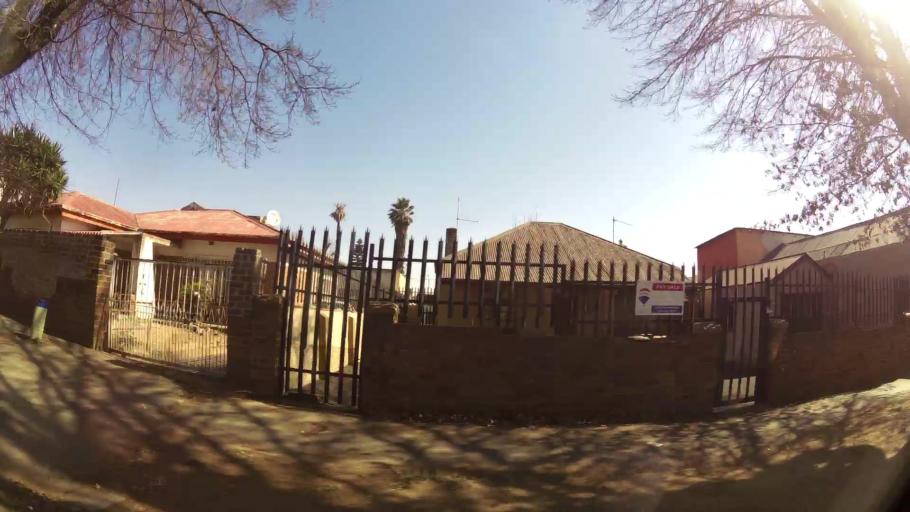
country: ZA
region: Gauteng
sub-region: City of Johannesburg Metropolitan Municipality
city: Johannesburg
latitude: -26.2412
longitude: 28.0732
